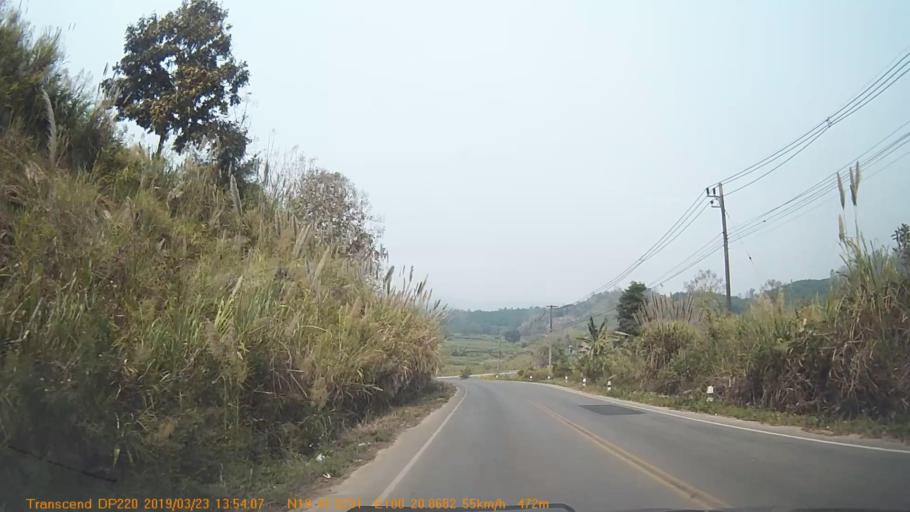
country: TH
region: Chiang Rai
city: Khun Tan
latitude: 19.7923
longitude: 100.3477
